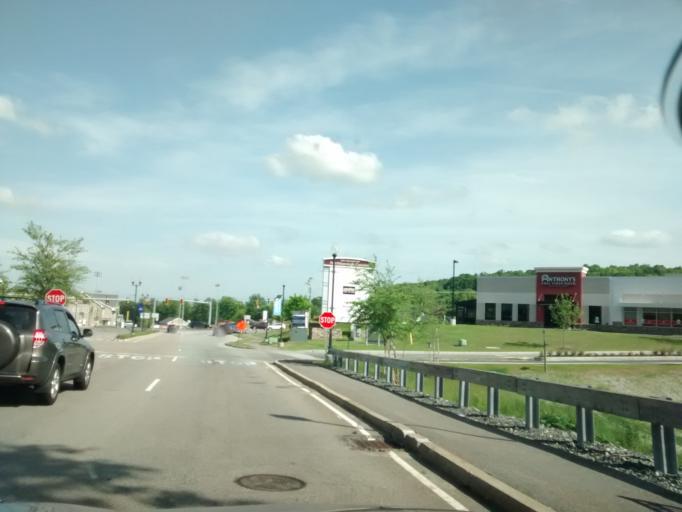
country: US
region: Massachusetts
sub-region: Worcester County
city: Northborough
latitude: 42.2866
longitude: -71.6698
